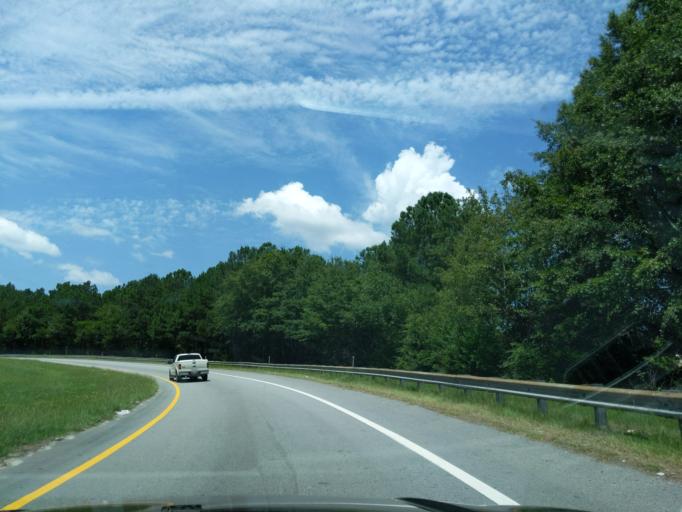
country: US
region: South Carolina
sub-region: Richland County
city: Dentsville
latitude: 34.0752
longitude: -80.9475
